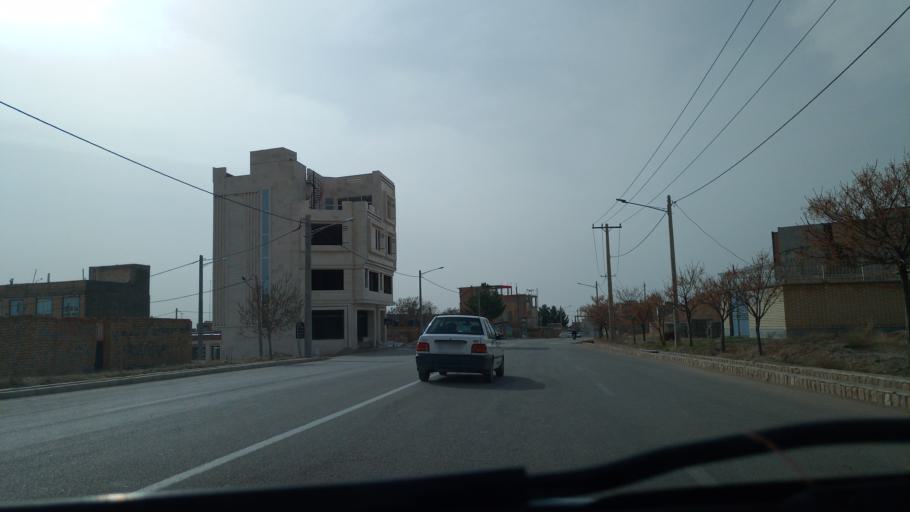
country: IR
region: Khorasan-e Shomali
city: Esfarayen
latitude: 37.0850
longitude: 57.5023
